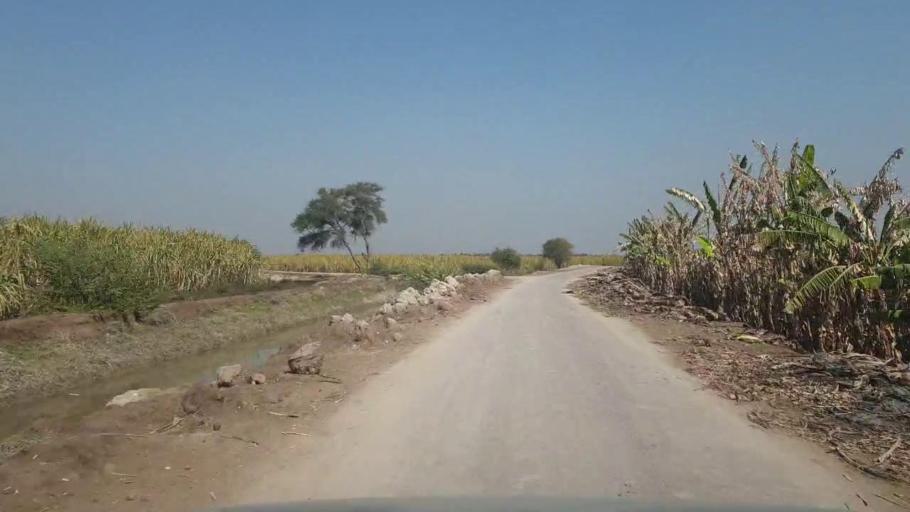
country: PK
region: Sindh
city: Chambar
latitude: 25.2413
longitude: 68.8531
